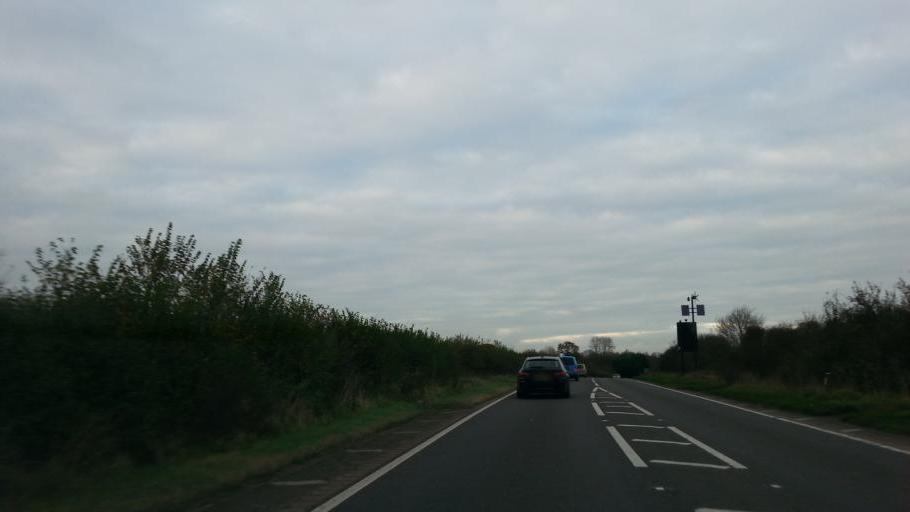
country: GB
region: England
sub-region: District of Rutland
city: Ketton
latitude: 52.5763
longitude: -0.5666
